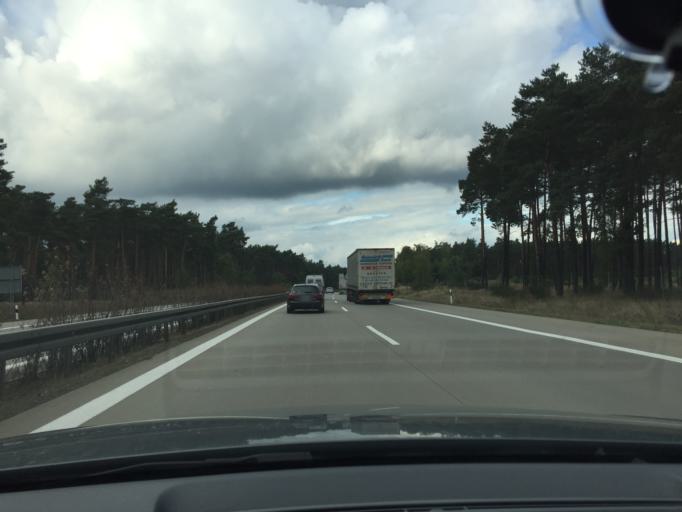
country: DE
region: Brandenburg
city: Kasel-Golzig
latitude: 51.9297
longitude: 13.7682
